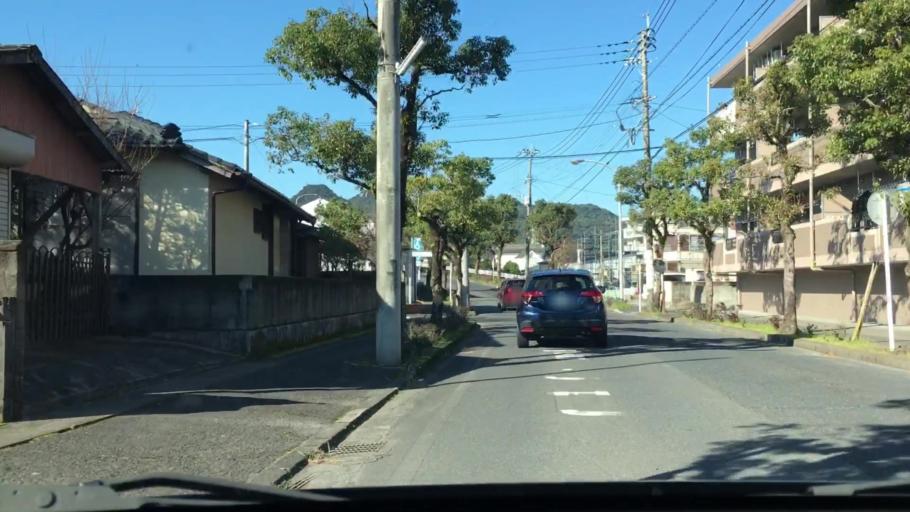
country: JP
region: Kagoshima
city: Kajiki
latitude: 31.7411
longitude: 130.6600
